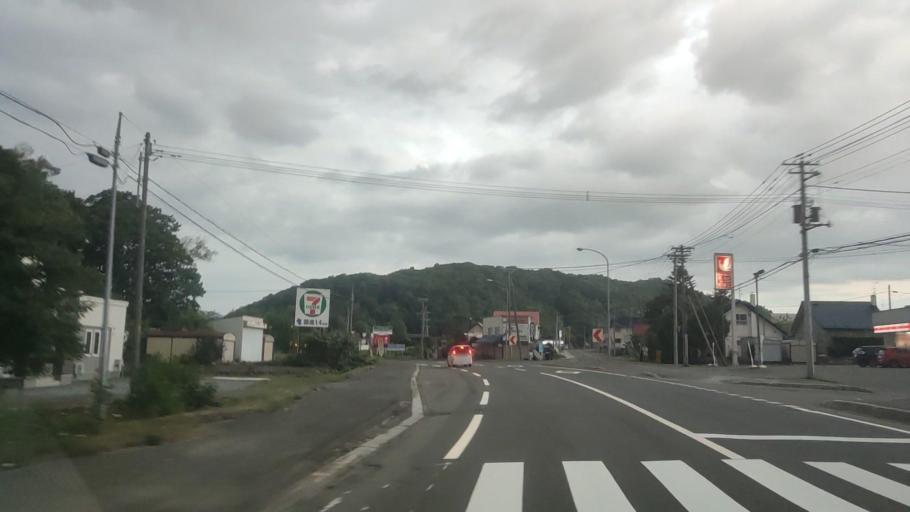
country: JP
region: Hokkaido
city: Shimo-furano
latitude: 43.3464
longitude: 142.3691
